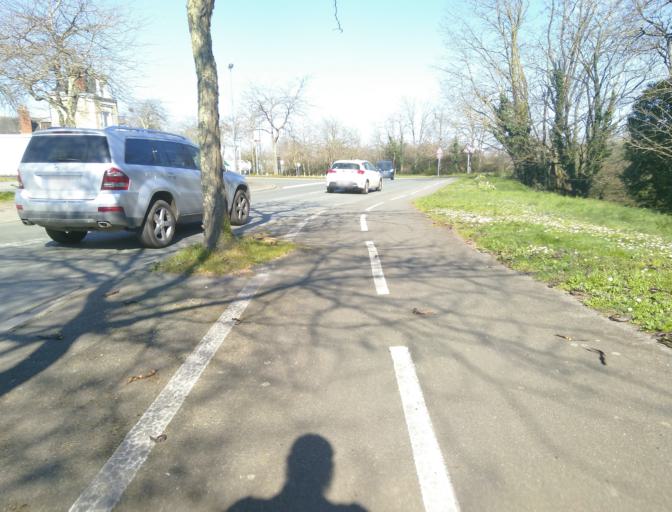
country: FR
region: Pays de la Loire
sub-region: Departement de Maine-et-Loire
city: Les Ponts-de-Ce
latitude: 47.4553
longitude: -0.5071
